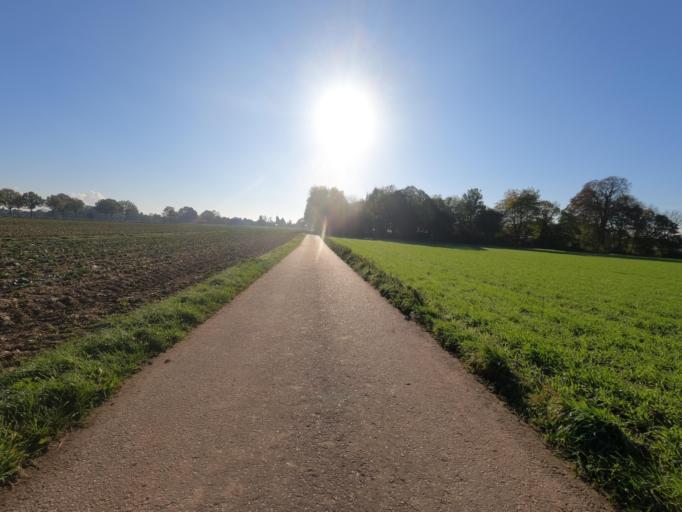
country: DE
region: North Rhine-Westphalia
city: Erkelenz
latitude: 51.0941
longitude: 6.3620
